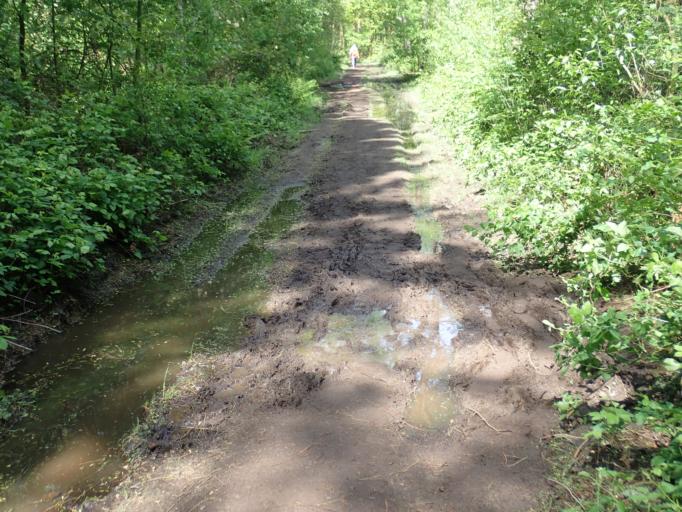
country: BE
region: Flanders
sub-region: Provincie Antwerpen
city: Lille
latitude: 51.2242
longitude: 4.8214
